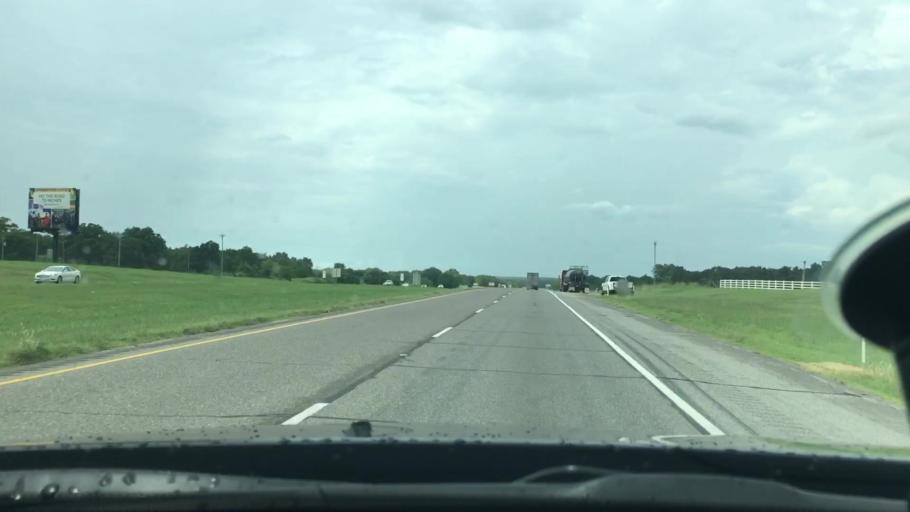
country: US
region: Oklahoma
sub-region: Murray County
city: Davis
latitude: 34.5080
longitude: -97.1750
